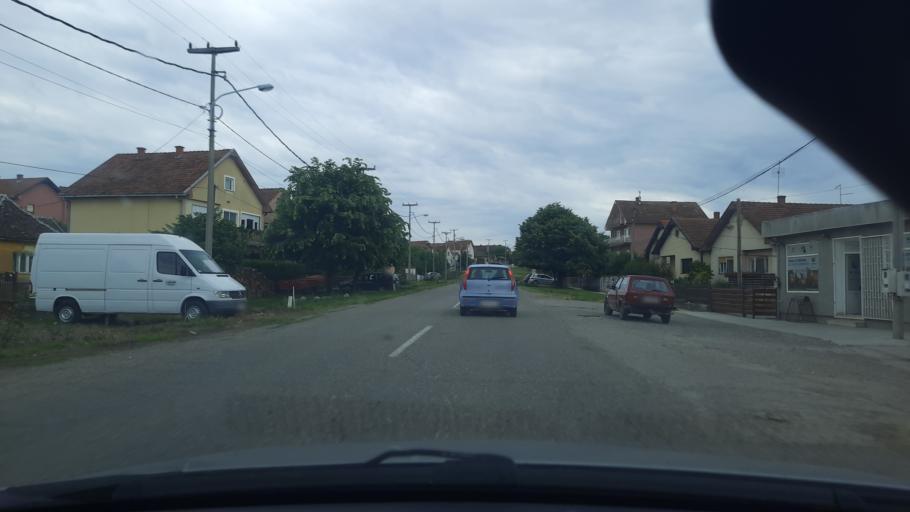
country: RS
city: Jevremovac
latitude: 44.7316
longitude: 19.6705
